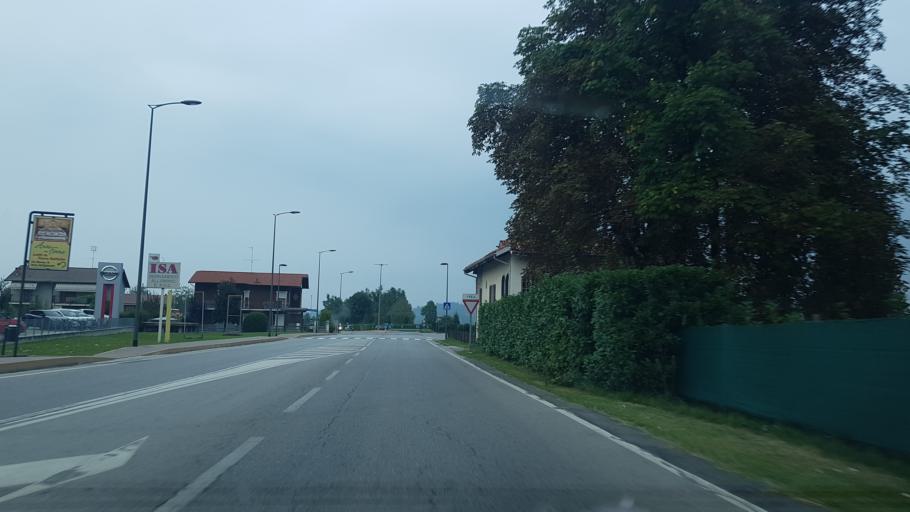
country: IT
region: Piedmont
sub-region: Provincia di Cuneo
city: Villanova Mondovi
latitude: 44.3537
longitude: 7.7839
